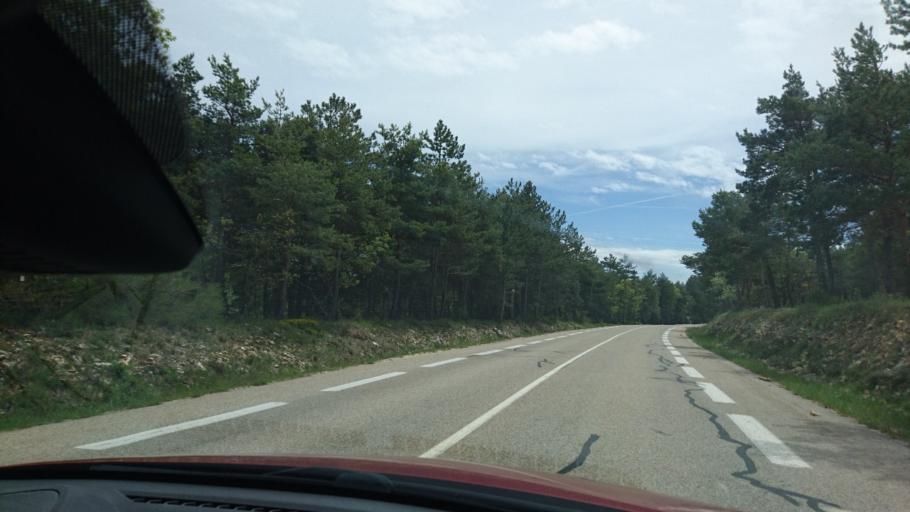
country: FR
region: Provence-Alpes-Cote d'Azur
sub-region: Departement du Vaucluse
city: Sault
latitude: 44.0894
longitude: 5.3539
